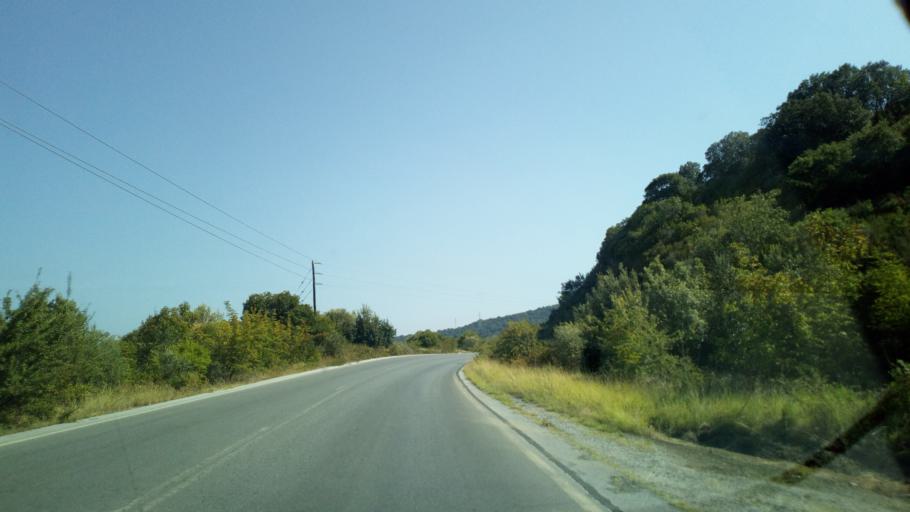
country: GR
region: Central Macedonia
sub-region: Nomos Thessalonikis
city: Stavros
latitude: 40.6446
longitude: 23.7471
